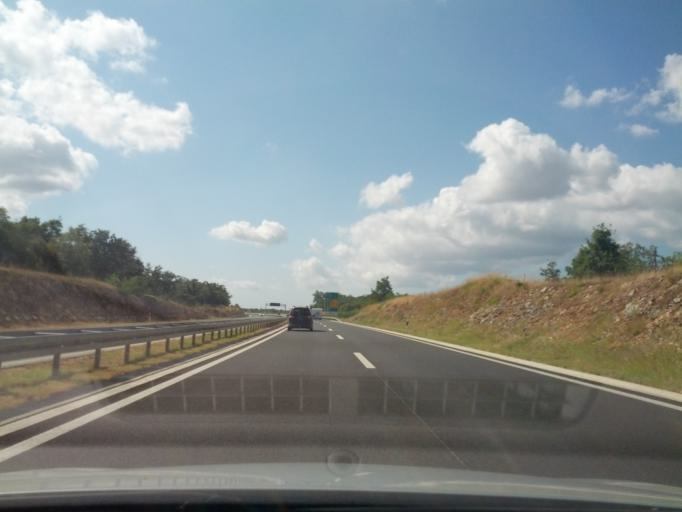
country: HR
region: Istarska
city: Vodnjan
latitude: 44.9990
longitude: 13.8381
